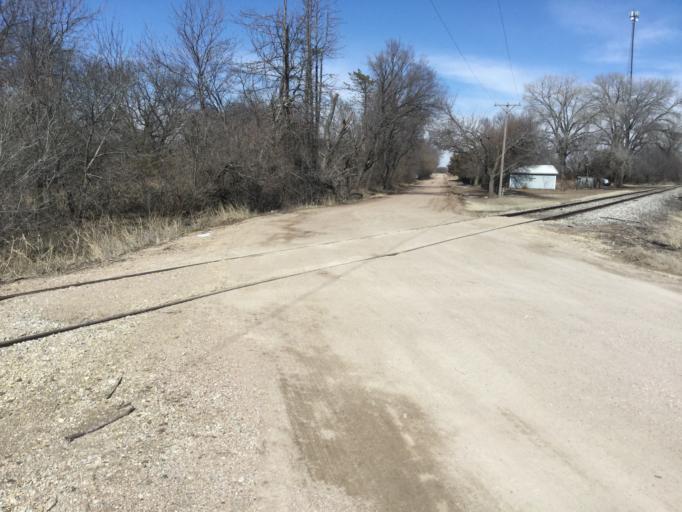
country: US
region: Kansas
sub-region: Sedgwick County
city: Clearwater
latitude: 37.4956
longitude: -97.5151
